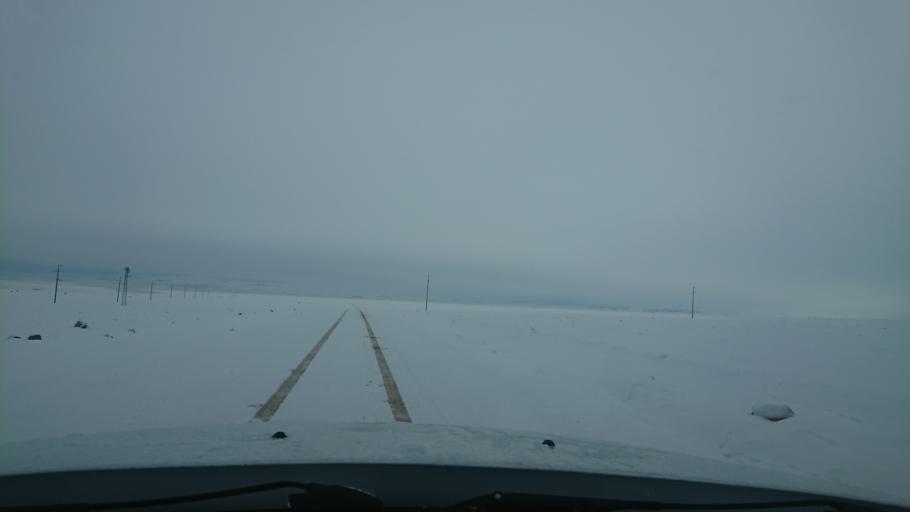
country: TR
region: Aksaray
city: Agacoren
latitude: 38.7224
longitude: 33.8666
